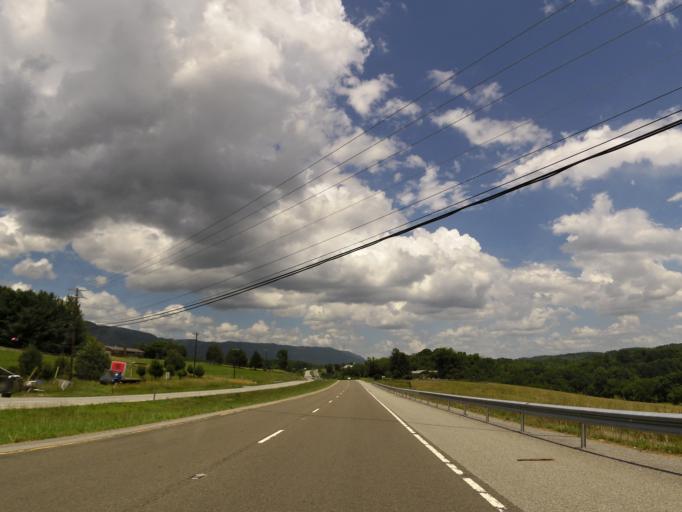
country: US
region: Tennessee
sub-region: Claiborne County
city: Harrogate
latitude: 36.6091
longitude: -83.5768
